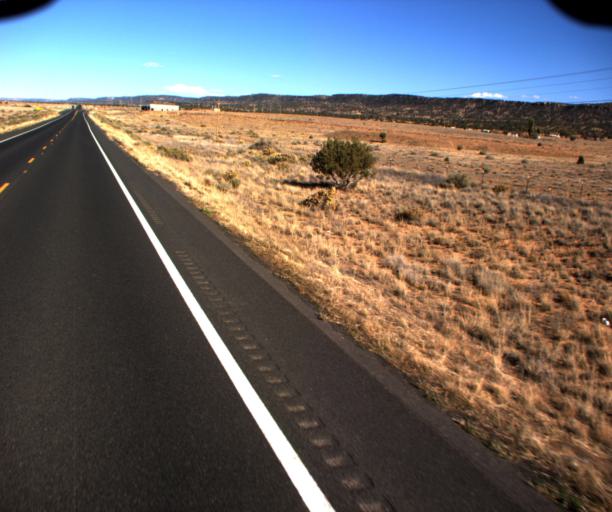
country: US
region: Arizona
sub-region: Coconino County
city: Kaibito
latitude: 36.4585
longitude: -110.6985
